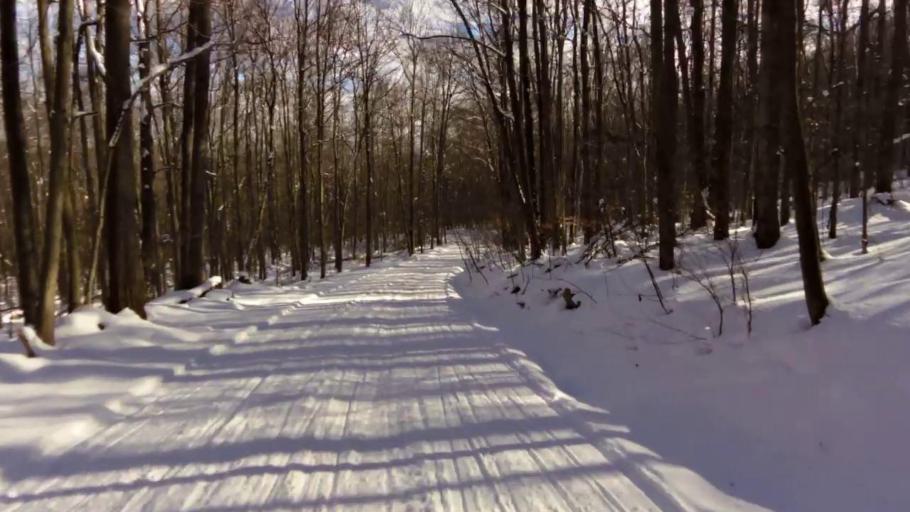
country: US
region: Pennsylvania
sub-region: McKean County
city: Foster Brook
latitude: 42.0656
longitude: -78.6612
